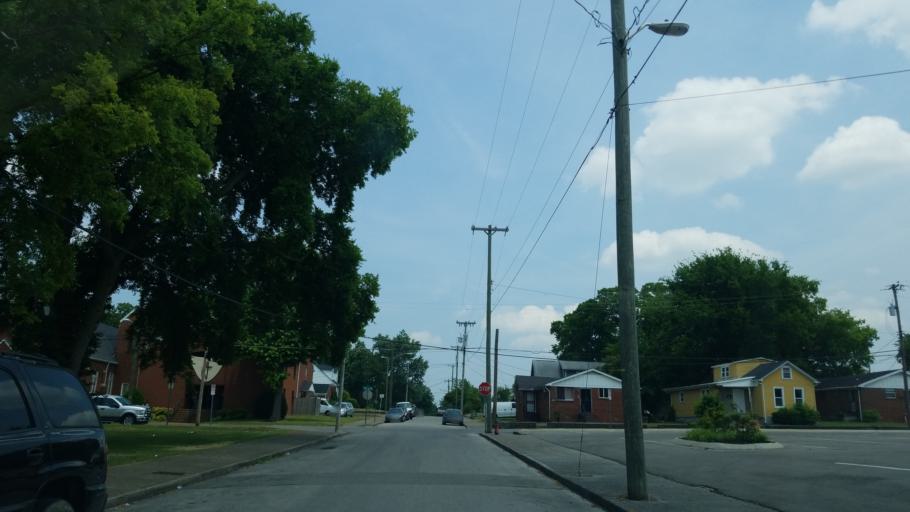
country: US
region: Tennessee
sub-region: Davidson County
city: Nashville
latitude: 36.1689
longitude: -86.8004
